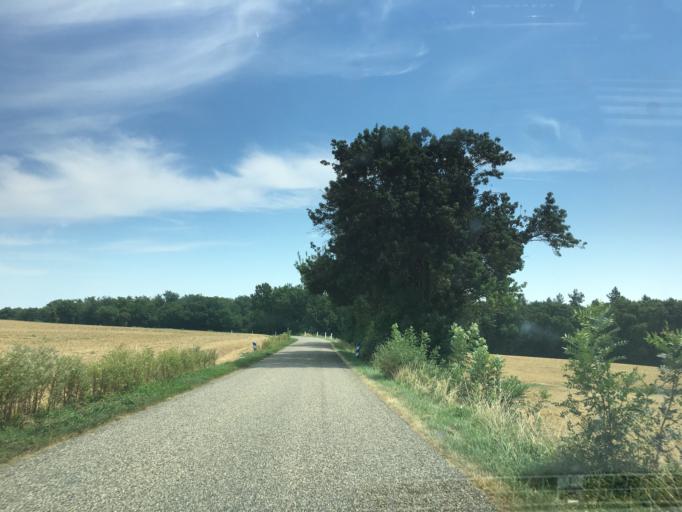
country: FR
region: Midi-Pyrenees
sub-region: Departement du Gers
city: Fleurance
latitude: 43.8161
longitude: 0.5710
